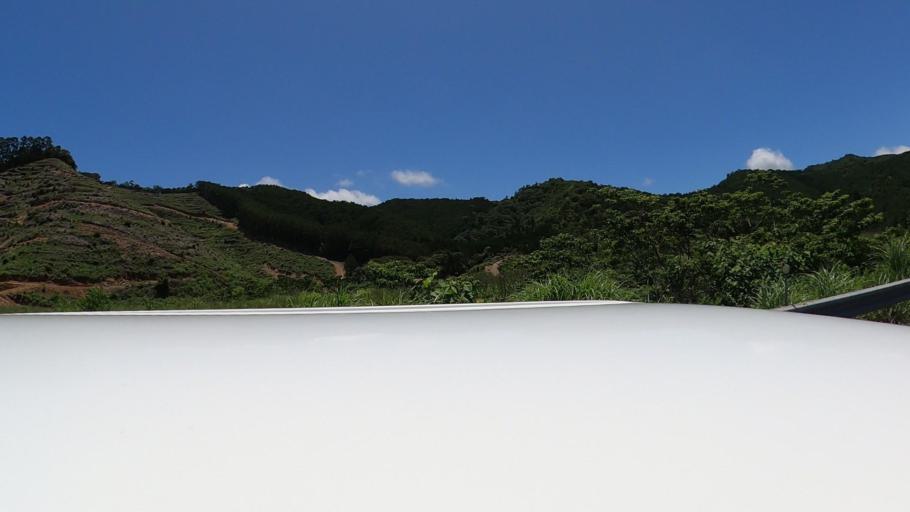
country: JP
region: Miyazaki
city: Nobeoka
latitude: 32.5434
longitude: 131.6506
